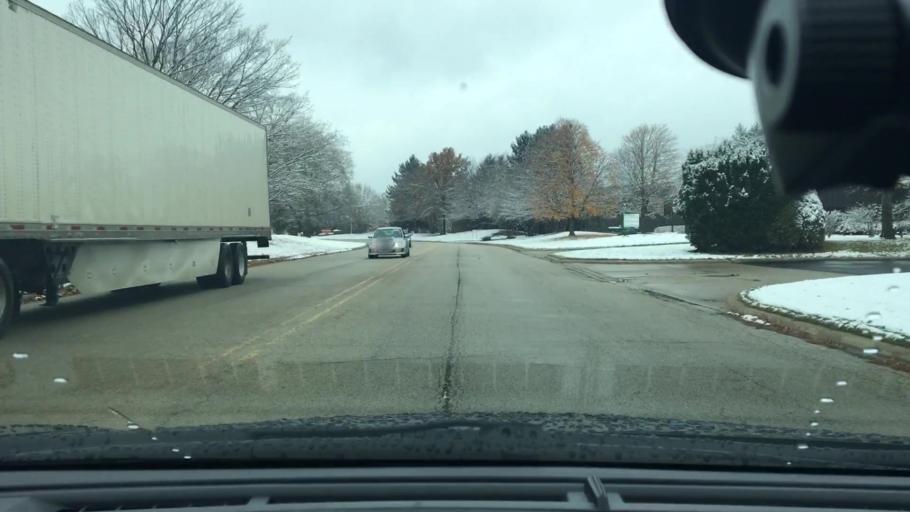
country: US
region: Illinois
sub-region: Lake County
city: Lincolnshire
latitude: 42.1889
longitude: -87.9358
